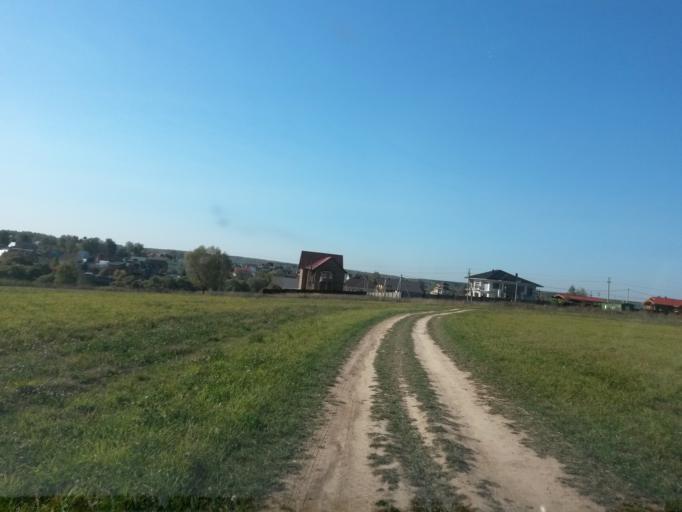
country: RU
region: Moskovskaya
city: Lyubuchany
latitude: 55.2590
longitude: 37.6136
